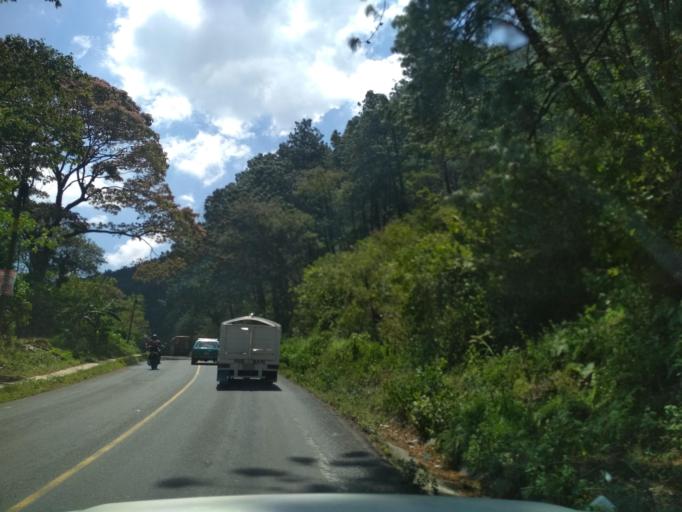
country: MX
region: Veracruz
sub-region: Tlilapan
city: Tonalixco
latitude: 18.7808
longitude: -97.0839
